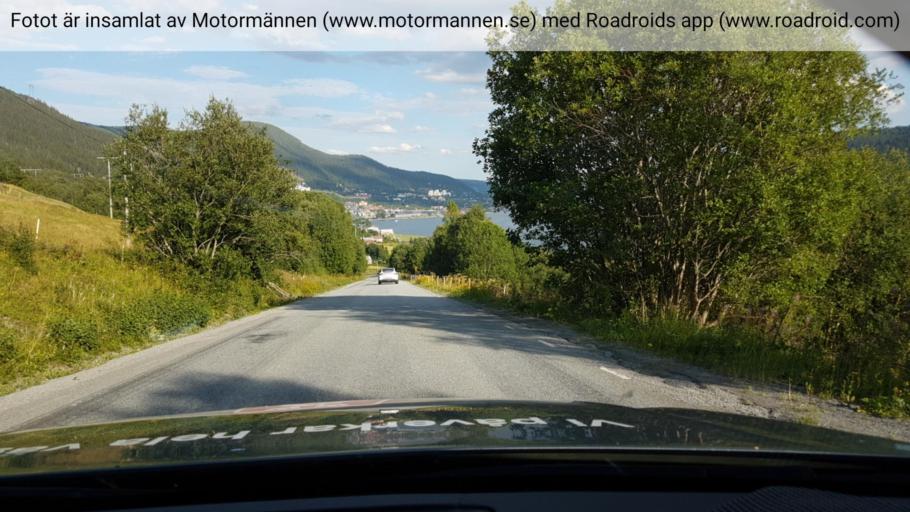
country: SE
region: Jaemtland
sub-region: Are Kommun
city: Are
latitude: 63.4067
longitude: 13.0328
